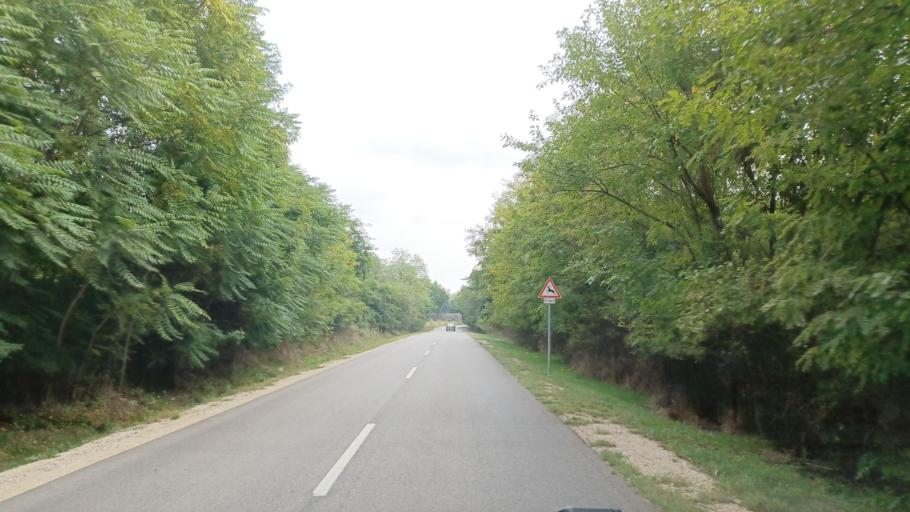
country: HU
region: Tolna
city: Pincehely
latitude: 46.6289
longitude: 18.4150
